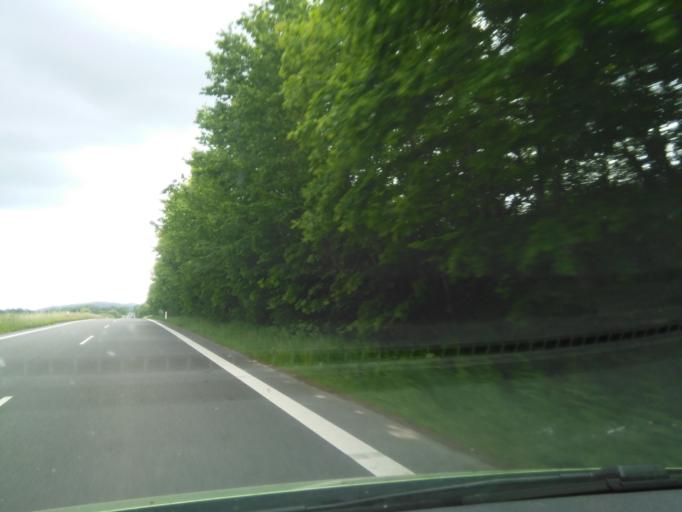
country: DK
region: Capital Region
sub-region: Bornholm Kommune
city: Akirkeby
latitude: 55.2201
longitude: 14.9096
